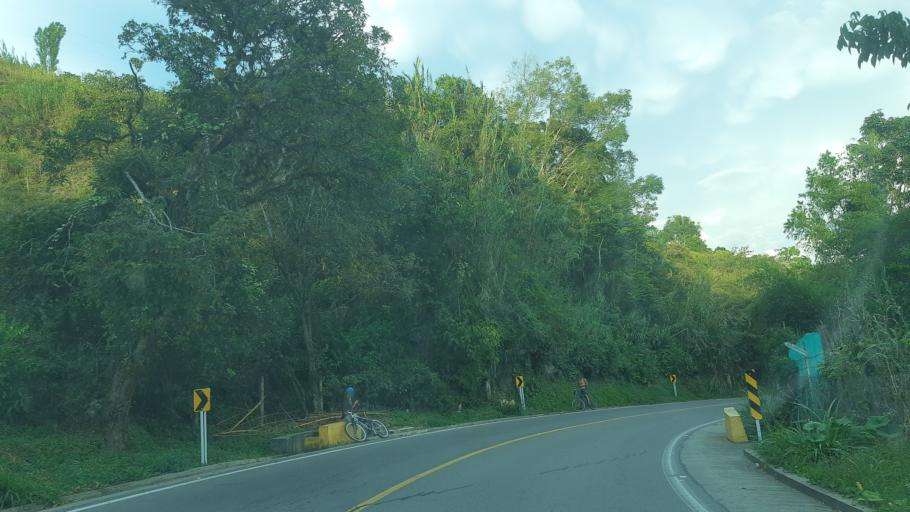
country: CO
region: Boyaca
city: Guateque
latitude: 5.0097
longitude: -73.4503
